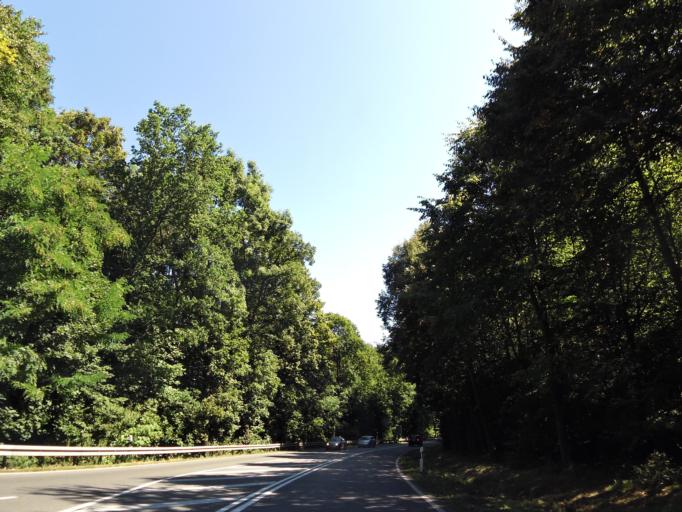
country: DE
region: Saxony
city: Konigstein
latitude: 50.9258
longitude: 14.0526
